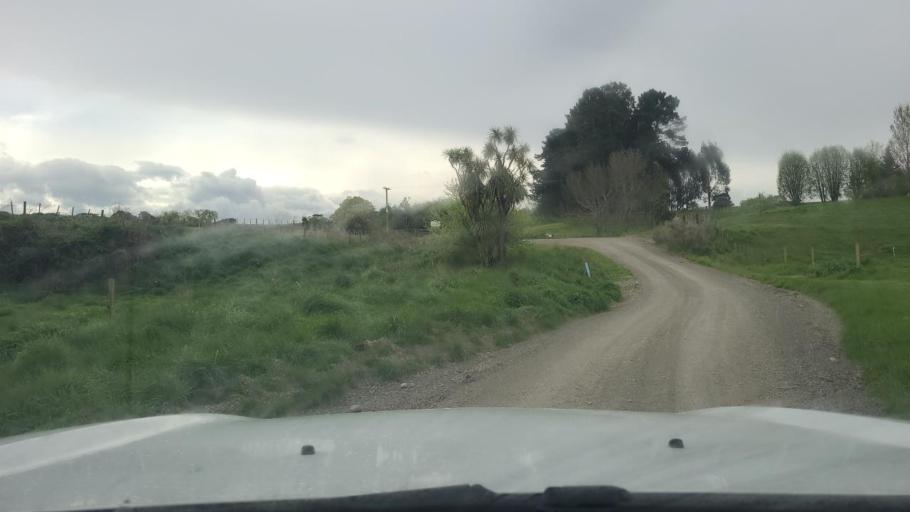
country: NZ
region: Wellington
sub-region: Masterton District
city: Masterton
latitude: -41.0531
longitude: 175.6303
